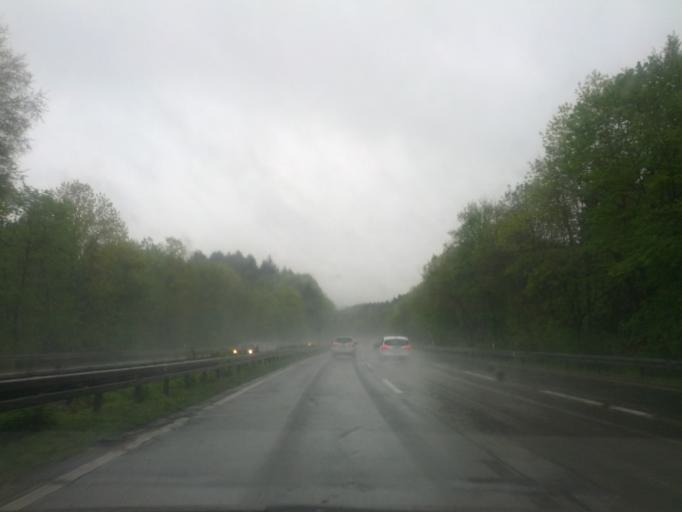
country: DE
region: North Rhine-Westphalia
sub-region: Regierungsbezirk Koln
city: Rosrath
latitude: 50.9548
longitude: 7.1947
